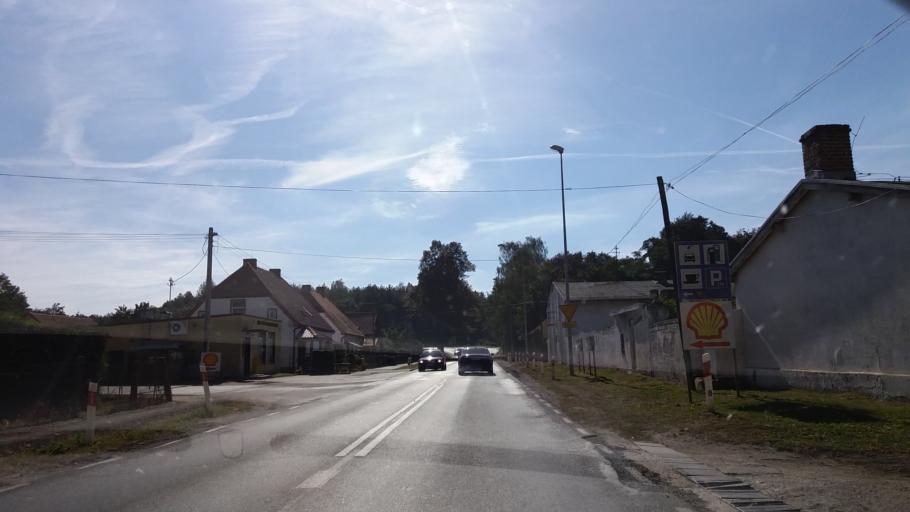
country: PL
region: Greater Poland Voivodeship
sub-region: Powiat miedzychodzki
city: Miedzychod
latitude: 52.5670
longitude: 15.8939
